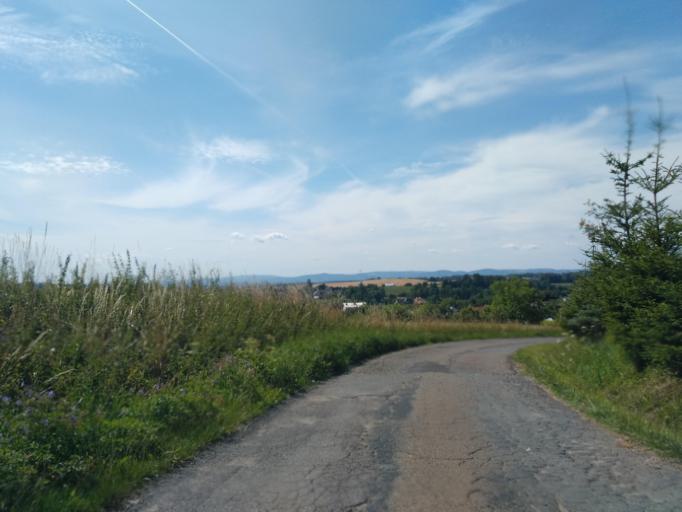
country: PL
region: Subcarpathian Voivodeship
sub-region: Powiat krosnienski
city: Korczyna
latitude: 49.7143
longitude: 21.8293
